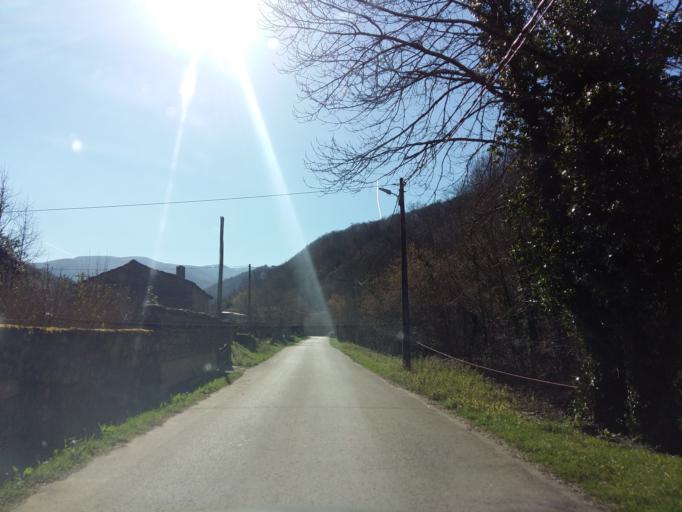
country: ES
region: Cantabria
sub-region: Provincia de Cantabria
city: Vega de Pas
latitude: 43.1495
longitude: -3.8025
